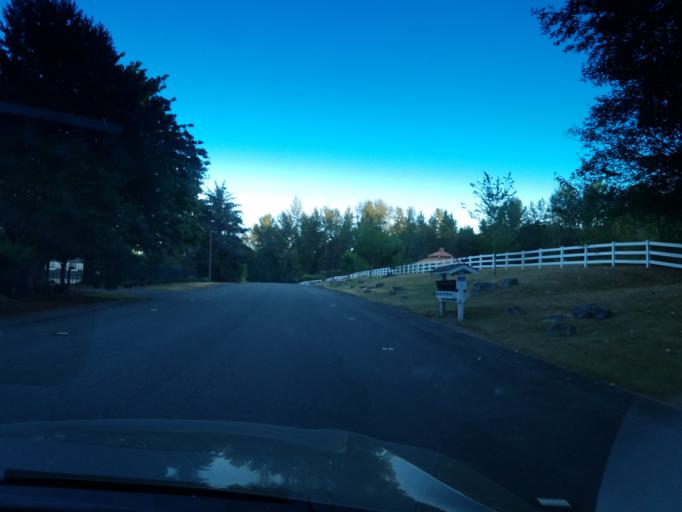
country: US
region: Washington
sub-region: King County
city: Ames Lake
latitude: 47.6422
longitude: -121.9866
